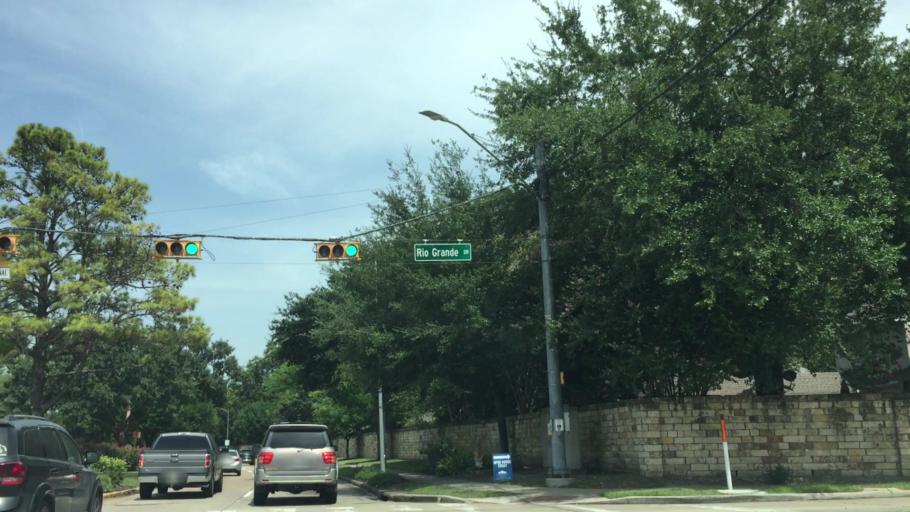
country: US
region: Texas
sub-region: Harris County
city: Jersey Village
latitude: 29.9087
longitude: -95.5736
